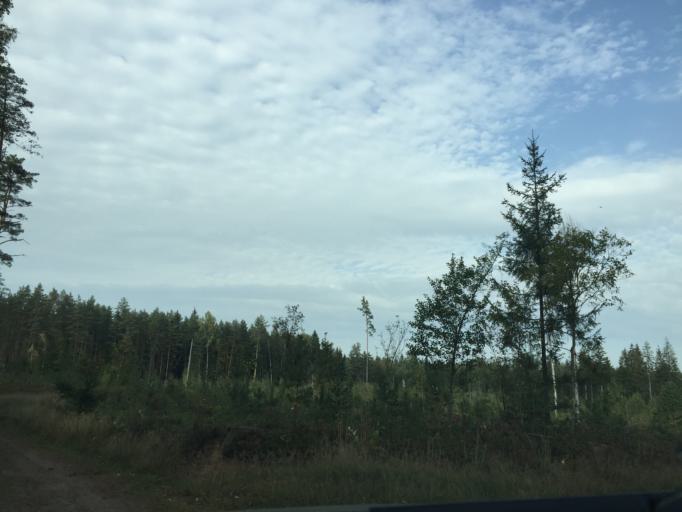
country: LV
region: Garkalne
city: Garkalne
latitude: 56.9444
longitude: 24.4344
